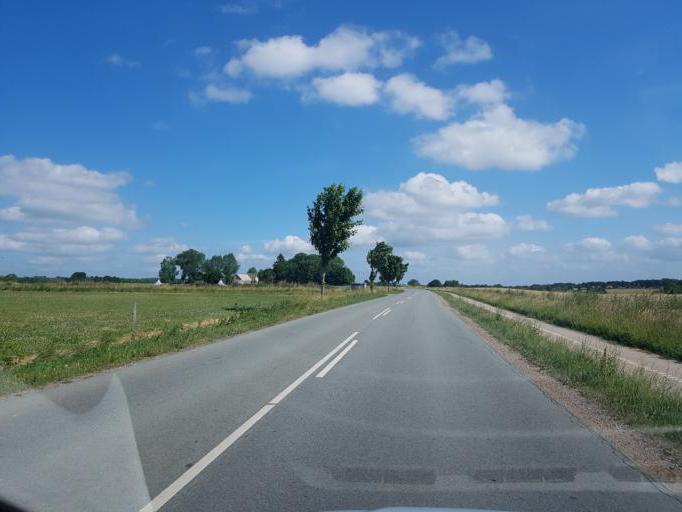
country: DK
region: Zealand
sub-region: Lejre Kommune
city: Lejre
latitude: 55.5861
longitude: 11.9691
